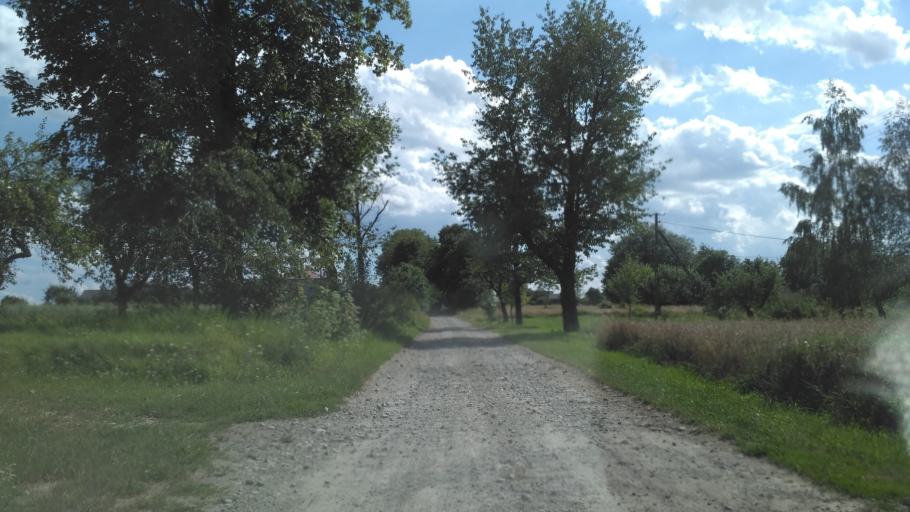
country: PL
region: Lublin Voivodeship
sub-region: Powiat leczynski
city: Milejow
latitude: 51.2045
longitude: 22.8693
